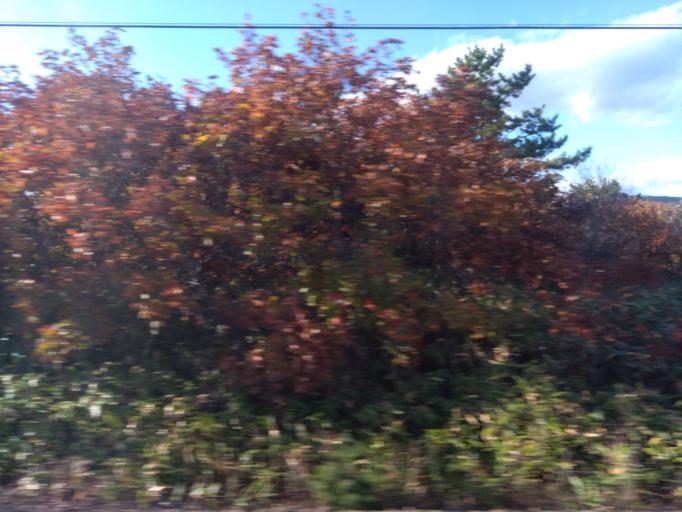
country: JP
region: Hokkaido
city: Niseko Town
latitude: 42.5718
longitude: 140.4437
